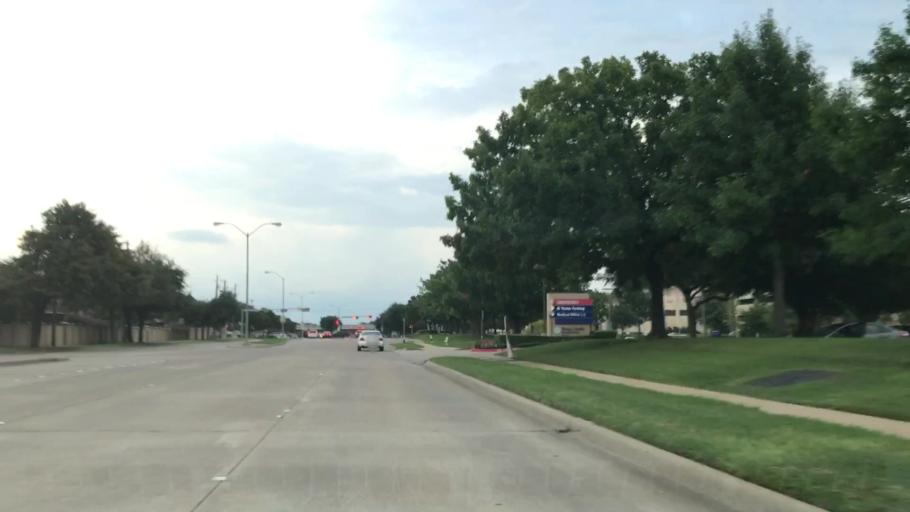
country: US
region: Texas
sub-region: Denton County
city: The Colony
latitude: 33.0452
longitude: -96.8353
